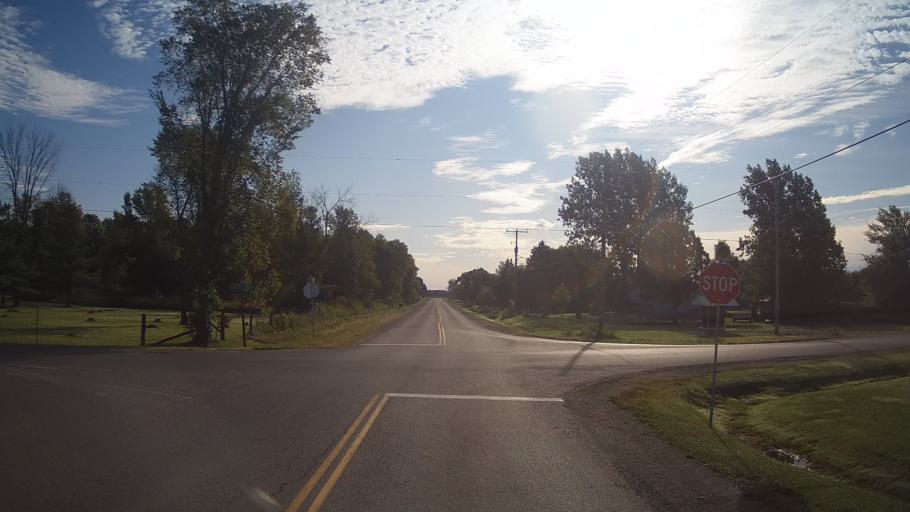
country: CA
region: Ontario
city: Gananoque
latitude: 44.4011
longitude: -76.0770
